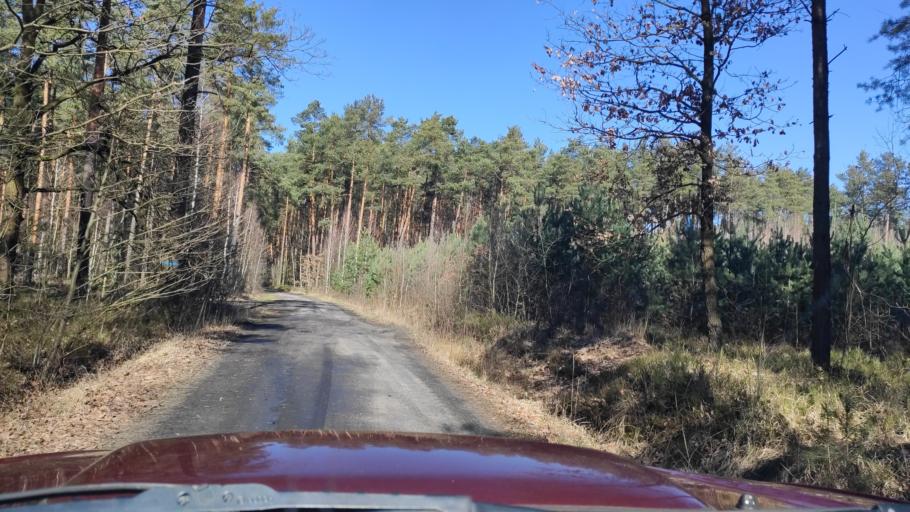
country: PL
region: Masovian Voivodeship
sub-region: Powiat kozienicki
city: Garbatka-Letnisko
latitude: 51.4346
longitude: 21.5465
